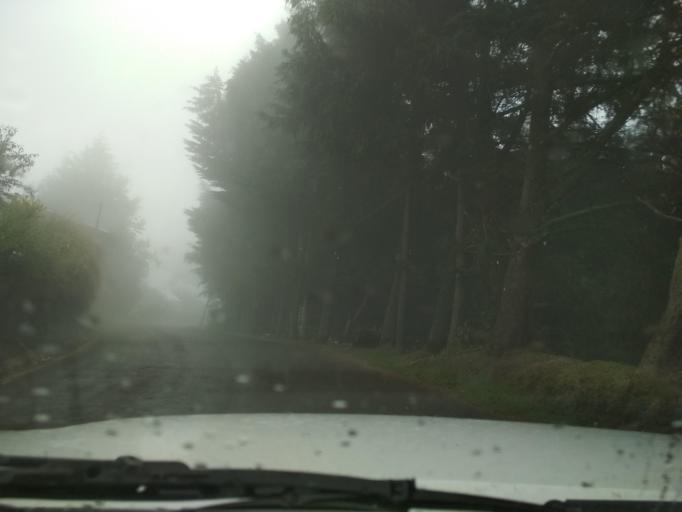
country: MX
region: Veracruz
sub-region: Mariano Escobedo
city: San Isidro el Berro
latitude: 18.9279
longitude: -97.2085
